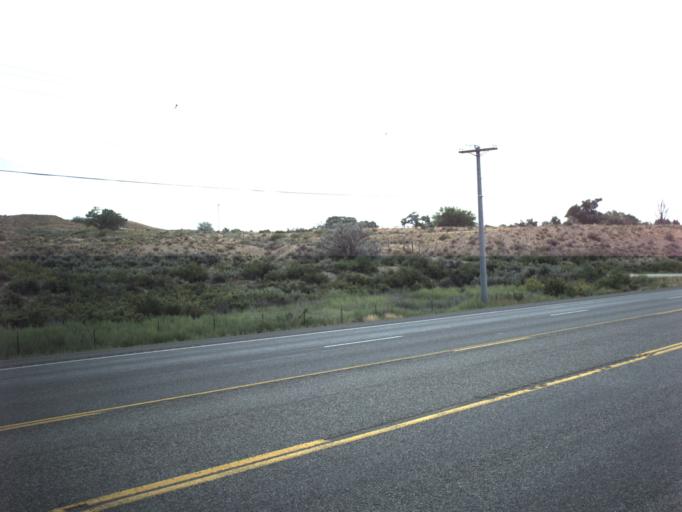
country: US
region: Utah
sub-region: Carbon County
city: Wellington
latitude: 39.5505
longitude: -110.7530
